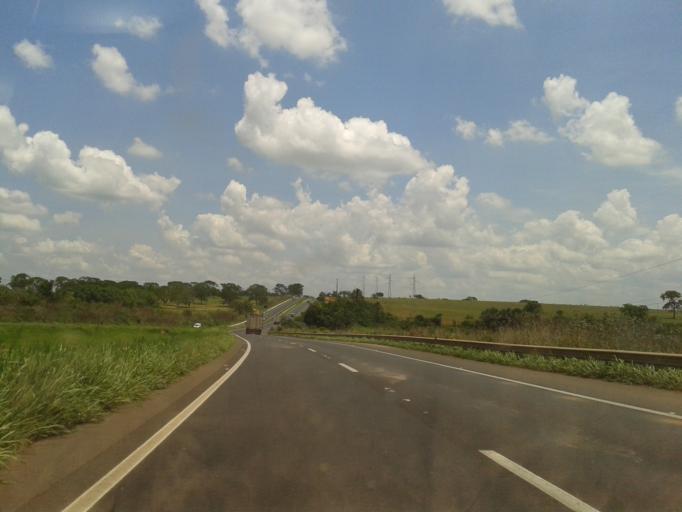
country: BR
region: Minas Gerais
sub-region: Uberlandia
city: Uberlandia
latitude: -18.8670
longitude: -48.5686
